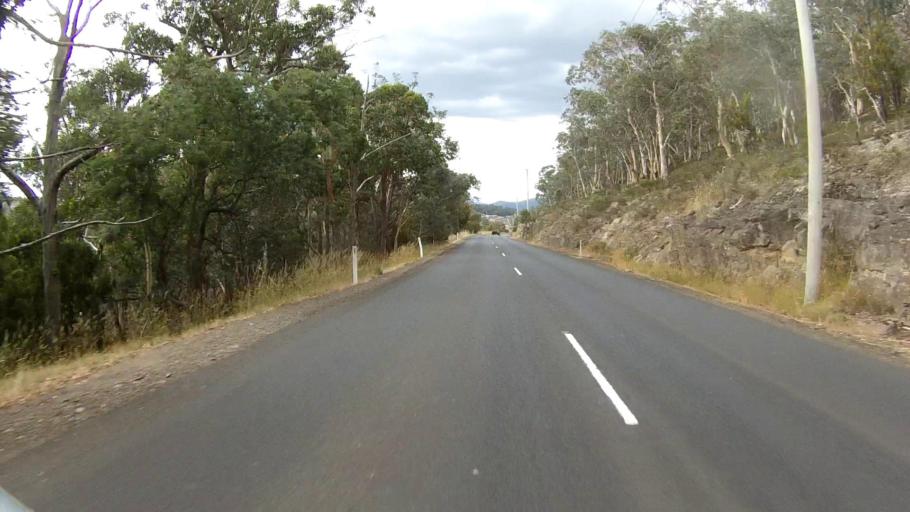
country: AU
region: Tasmania
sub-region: Hobart
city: Dynnyrne
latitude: -42.9026
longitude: 147.2906
